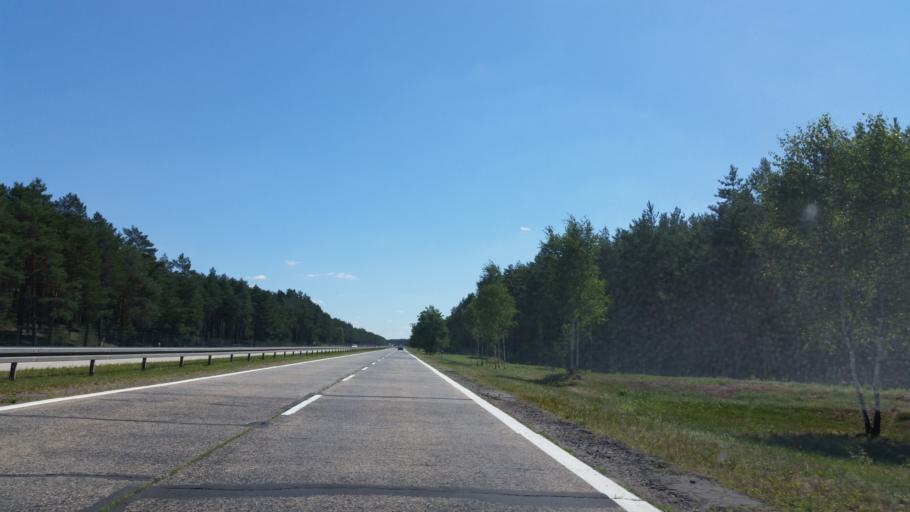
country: PL
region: Lubusz
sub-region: Powiat zaganski
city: Malomice
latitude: 51.4453
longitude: 15.3460
